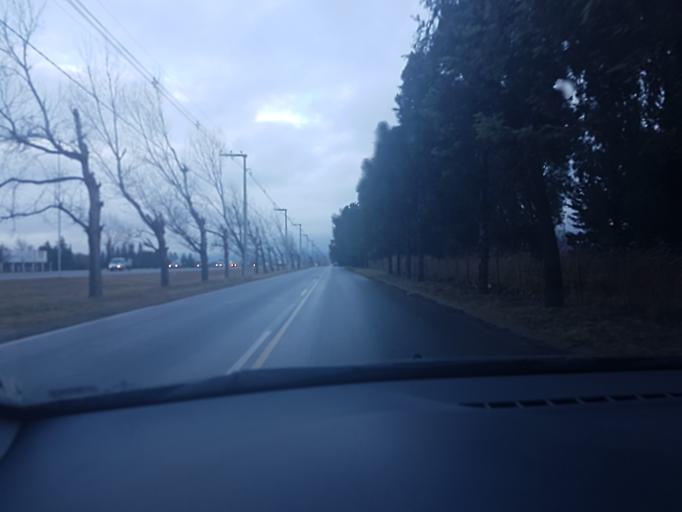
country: AR
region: Cordoba
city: Villa Allende
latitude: -31.3025
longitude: -64.2431
